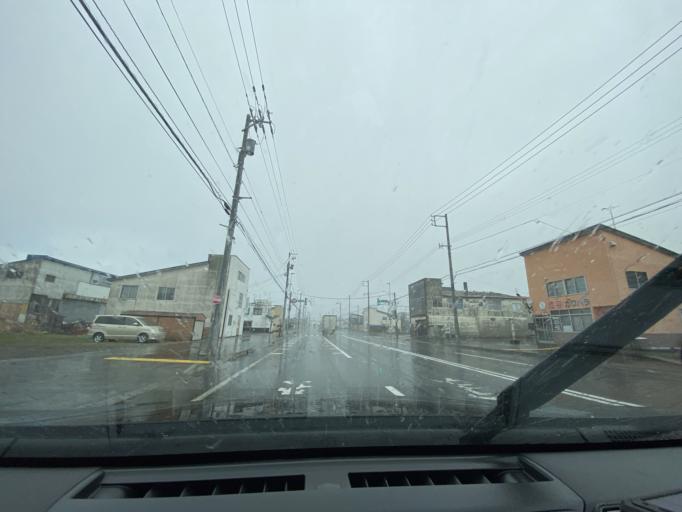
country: JP
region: Hokkaido
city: Takikawa
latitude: 43.6262
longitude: 141.9415
